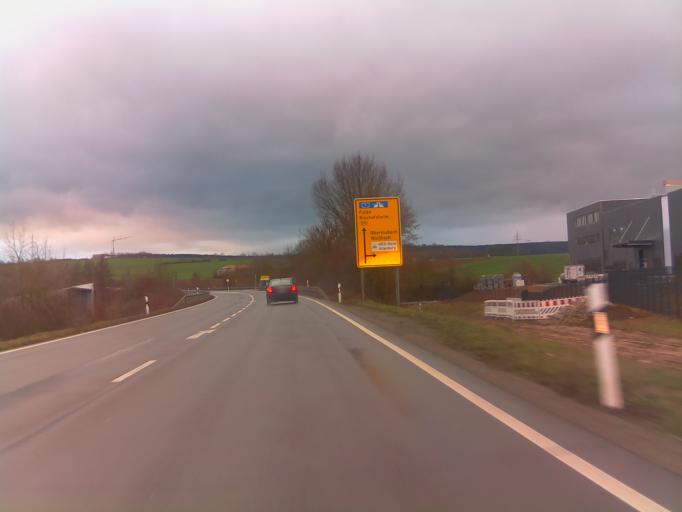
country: DE
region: Bavaria
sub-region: Regierungsbezirk Unterfranken
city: Bad Neustadt an der Saale
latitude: 50.3387
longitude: 10.2224
